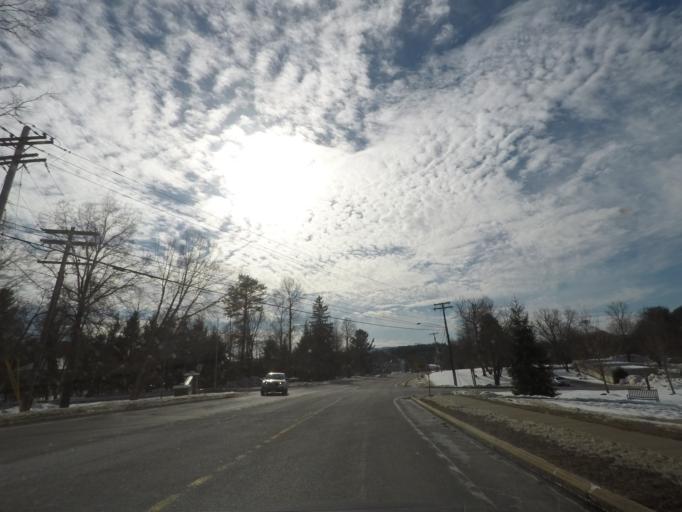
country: US
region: New York
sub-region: Albany County
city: Westmere
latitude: 42.6934
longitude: -73.8918
